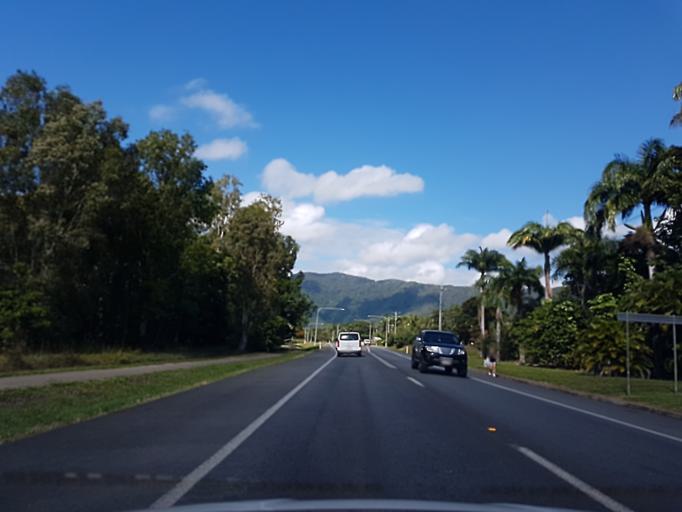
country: AU
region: Queensland
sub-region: Cairns
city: Trinity Beach
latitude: -16.7804
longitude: 145.6741
